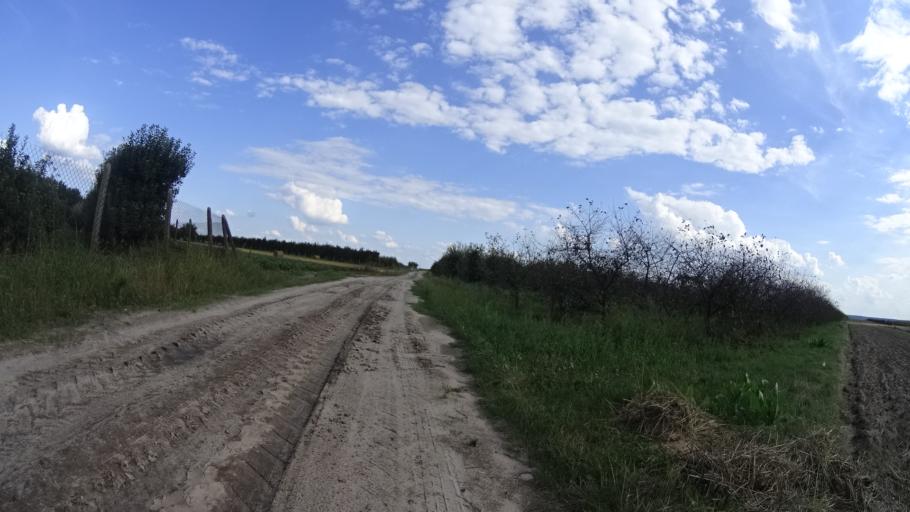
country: PL
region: Masovian Voivodeship
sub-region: Powiat bialobrzeski
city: Wysmierzyce
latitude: 51.6725
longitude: 20.7981
